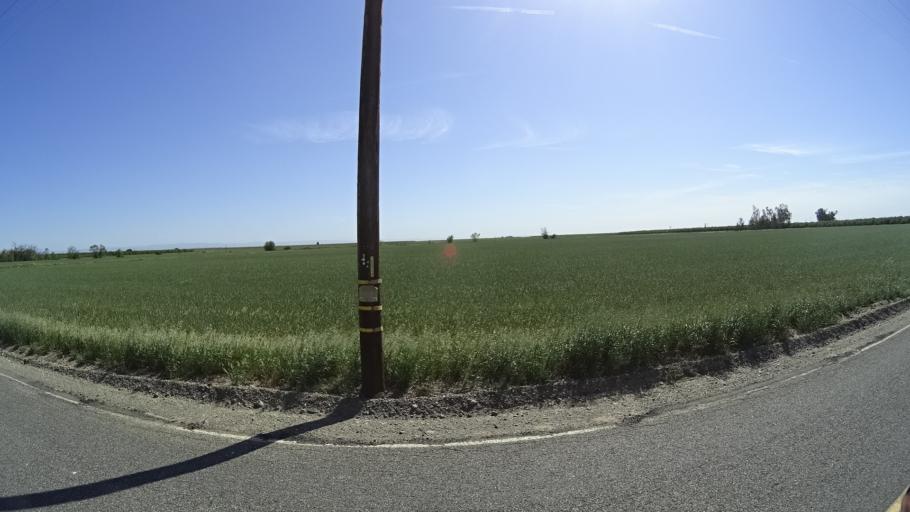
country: US
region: California
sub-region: Glenn County
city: Willows
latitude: 39.6343
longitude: -122.1786
